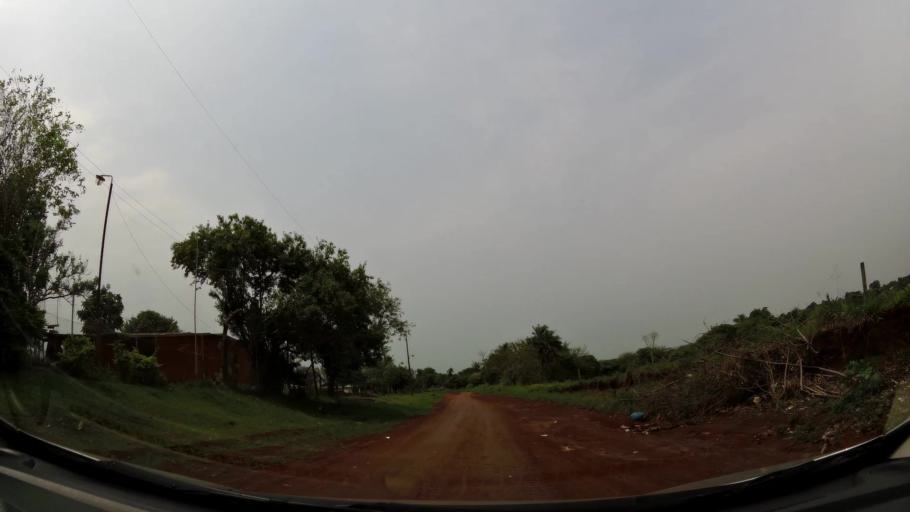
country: PY
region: Alto Parana
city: Presidente Franco
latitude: -25.5594
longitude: -54.6400
